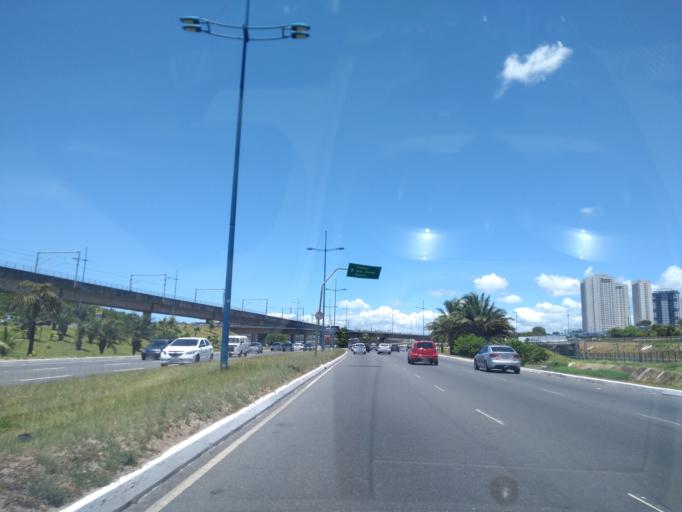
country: BR
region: Bahia
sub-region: Salvador
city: Salvador
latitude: -12.9743
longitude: -38.4769
